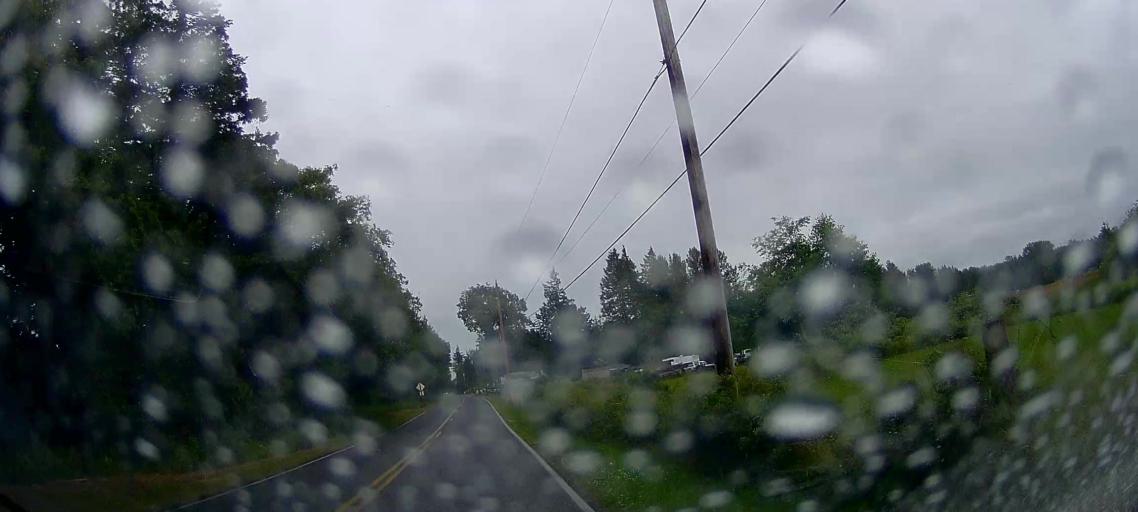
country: US
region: Washington
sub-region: Whatcom County
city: Marietta
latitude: 48.8009
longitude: -122.5758
